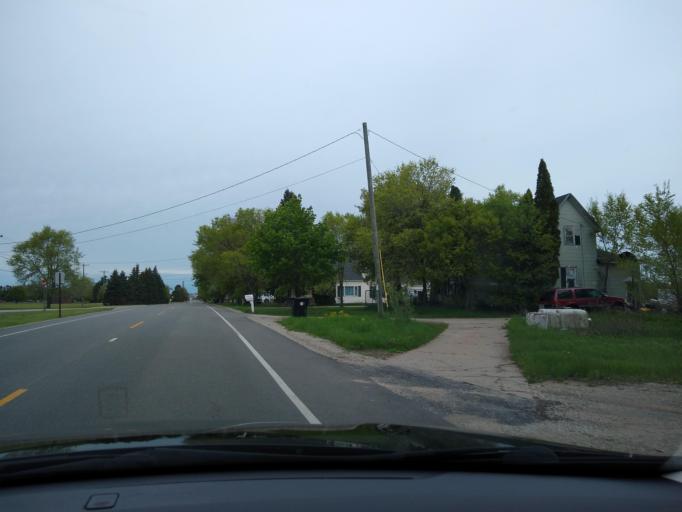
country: US
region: Michigan
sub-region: Delta County
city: Escanaba
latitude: 45.7826
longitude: -87.0758
